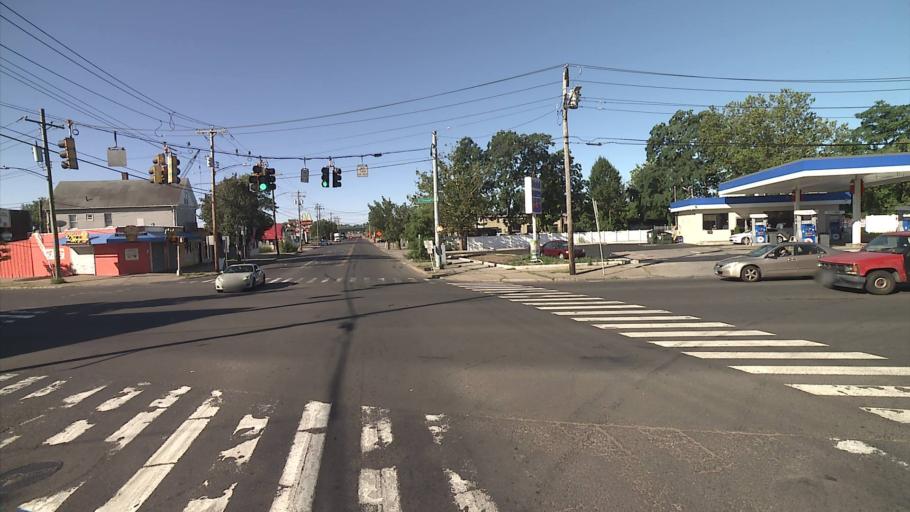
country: US
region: Connecticut
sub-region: New Haven County
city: West Haven
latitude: 41.2865
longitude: -72.9361
